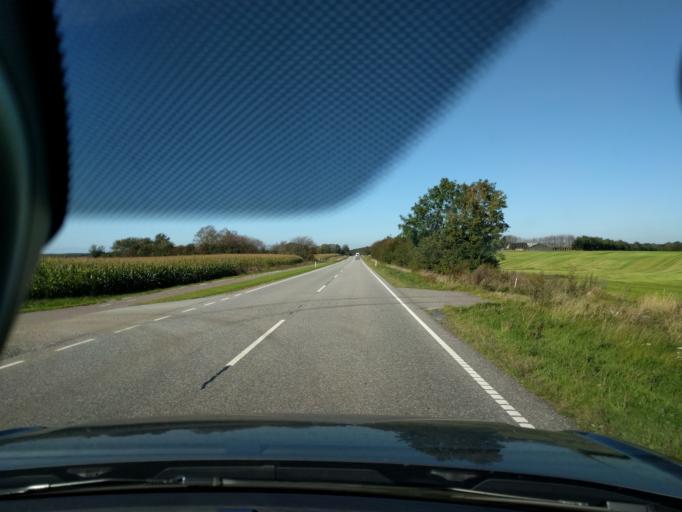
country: DK
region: North Denmark
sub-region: Mariagerfjord Kommune
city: Hobro
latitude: 56.6908
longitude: 9.6528
